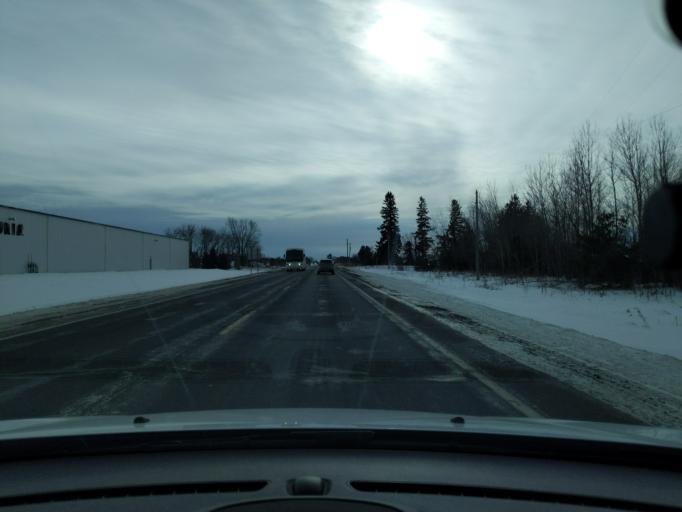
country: US
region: Wisconsin
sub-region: Barron County
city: Turtle Lake
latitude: 45.3896
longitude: -92.1666
